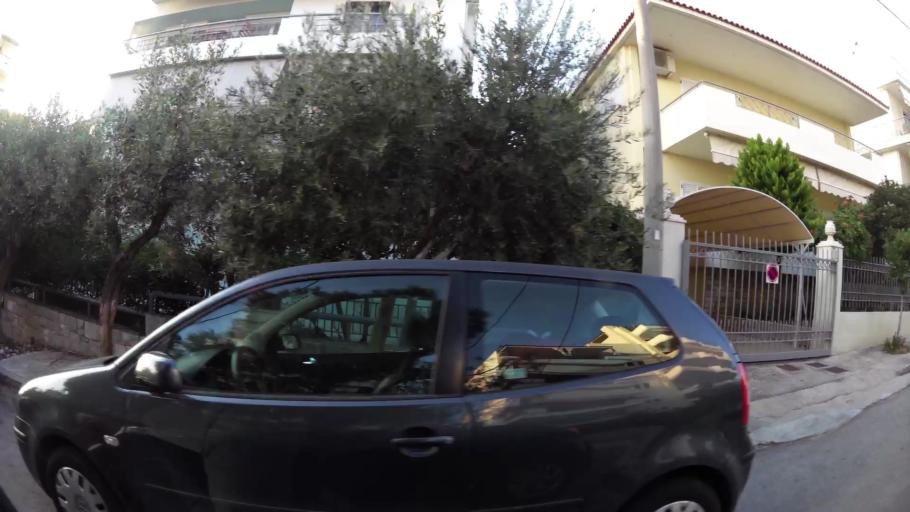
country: GR
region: Attica
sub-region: Nomarchia Athinas
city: Glyfada
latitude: 37.8864
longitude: 23.7706
